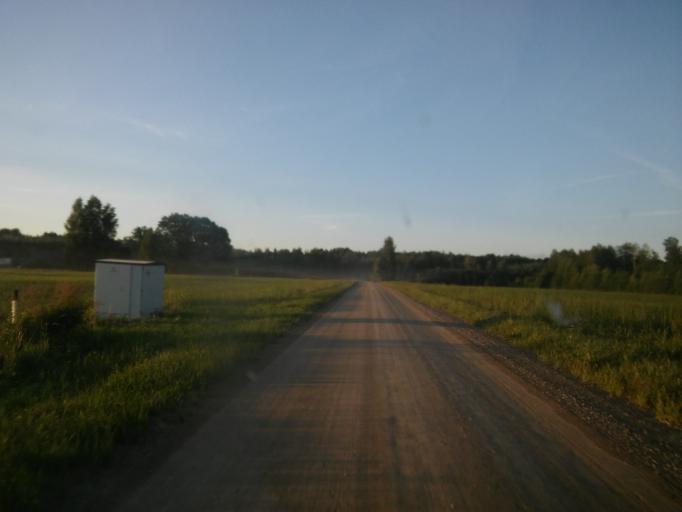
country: EE
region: Viljandimaa
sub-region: Abja vald
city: Abja-Paluoja
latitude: 58.2598
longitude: 25.3219
